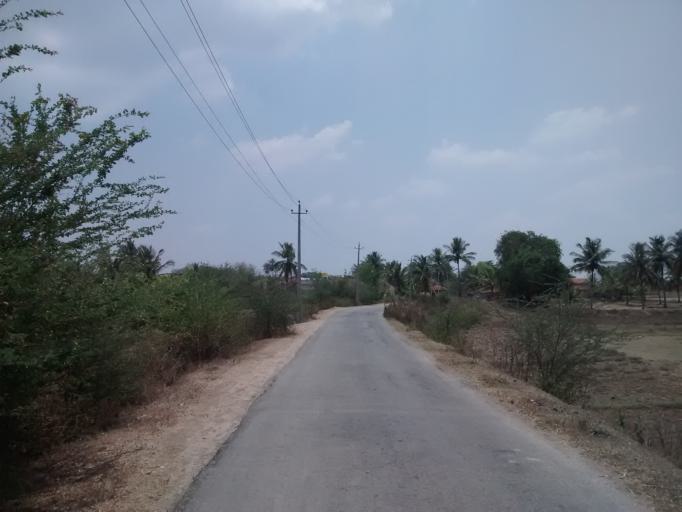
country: IN
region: Karnataka
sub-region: Hassan
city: Hassan
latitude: 12.9495
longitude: 76.1560
